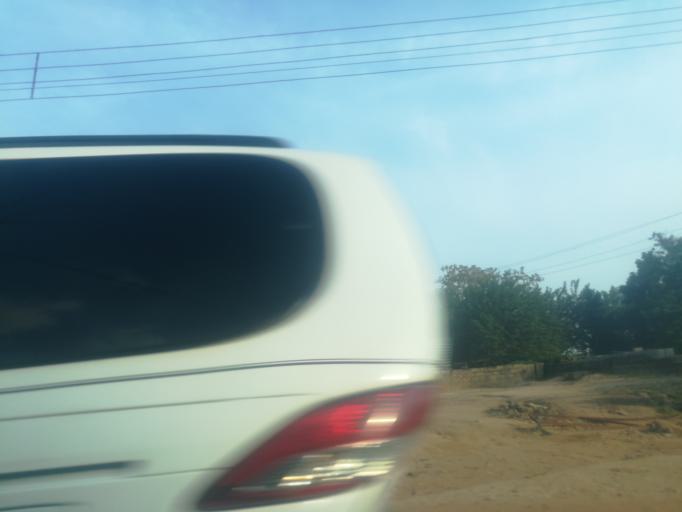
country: NG
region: Ogun
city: Abeokuta
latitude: 7.1249
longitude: 3.3237
